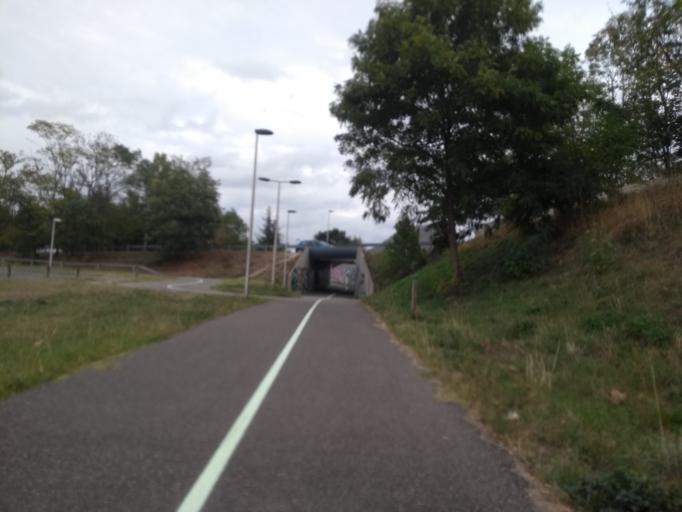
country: FR
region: Aquitaine
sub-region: Departement de la Gironde
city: Canejan
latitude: 44.7882
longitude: -0.6364
